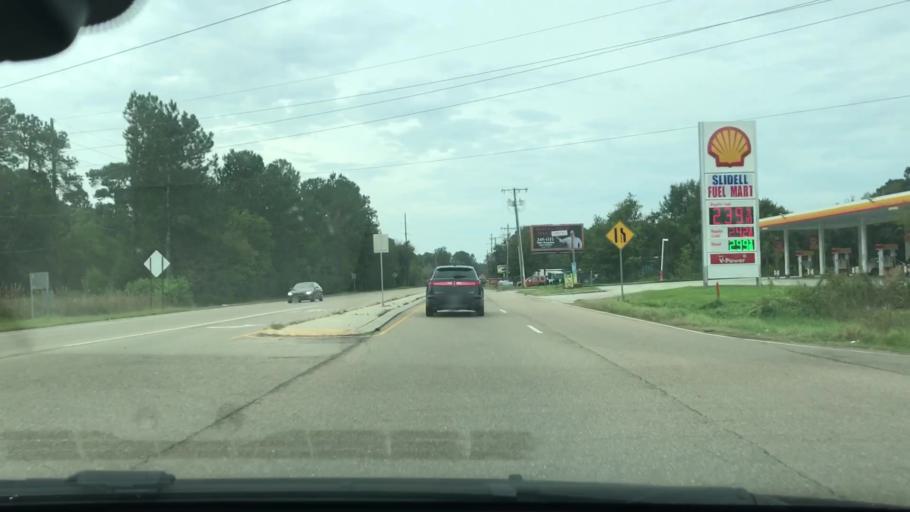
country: US
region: Louisiana
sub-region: Saint Tammany Parish
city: Slidell
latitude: 30.3062
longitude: -89.7723
